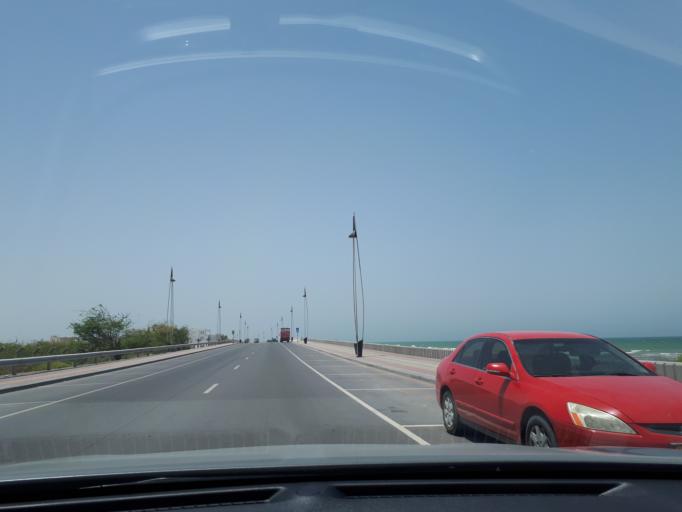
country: OM
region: Muhafazat Masqat
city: As Sib al Jadidah
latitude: 23.6522
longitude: 58.2310
